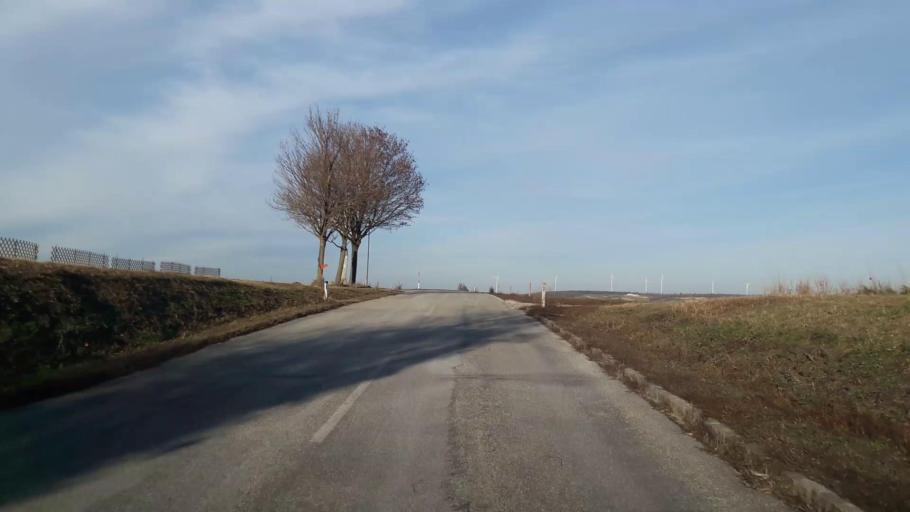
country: AT
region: Lower Austria
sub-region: Politischer Bezirk Ganserndorf
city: Gross-Schweinbarth
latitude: 48.3921
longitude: 16.6326
